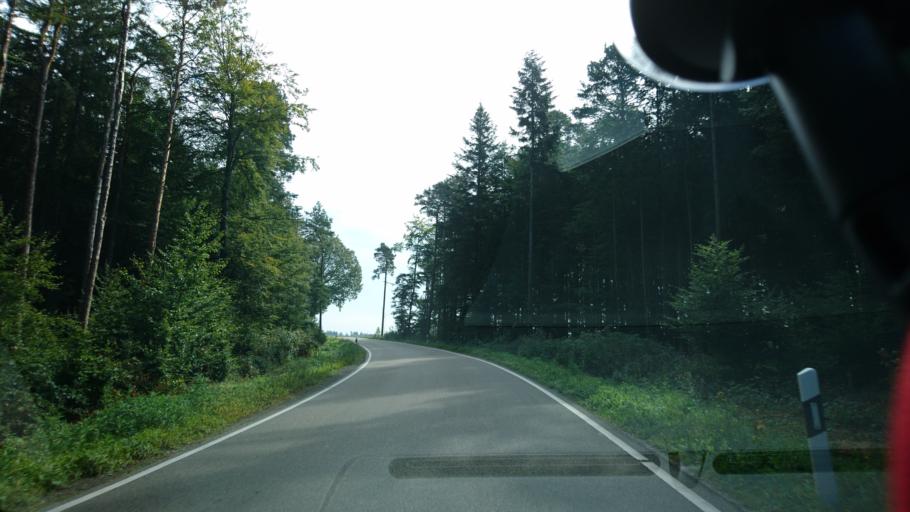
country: DE
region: Baden-Wuerttemberg
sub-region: Regierungsbezirk Stuttgart
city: Mainhardt
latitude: 49.0873
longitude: 9.5929
